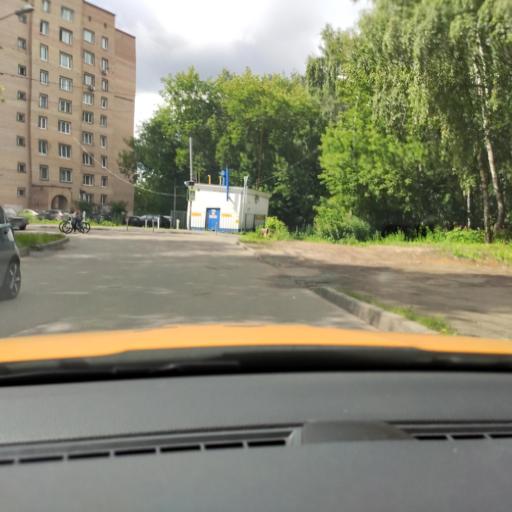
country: RU
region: Moskovskaya
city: Balashikha
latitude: 55.7997
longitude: 37.9539
